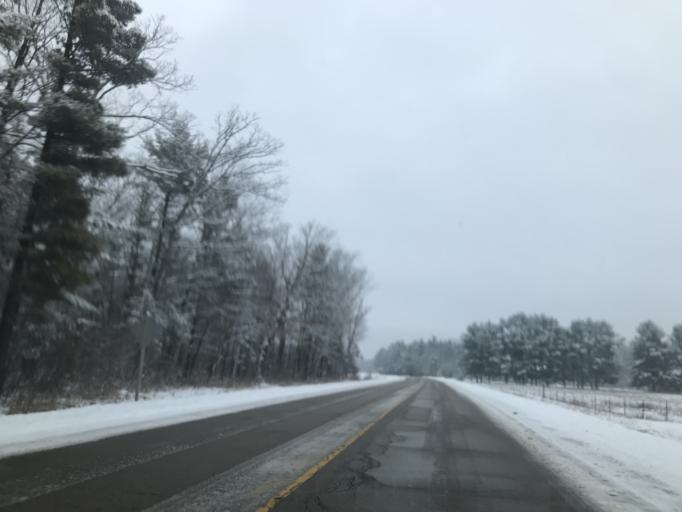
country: US
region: Wisconsin
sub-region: Oconto County
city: Oconto Falls
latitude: 44.8622
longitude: -88.1141
